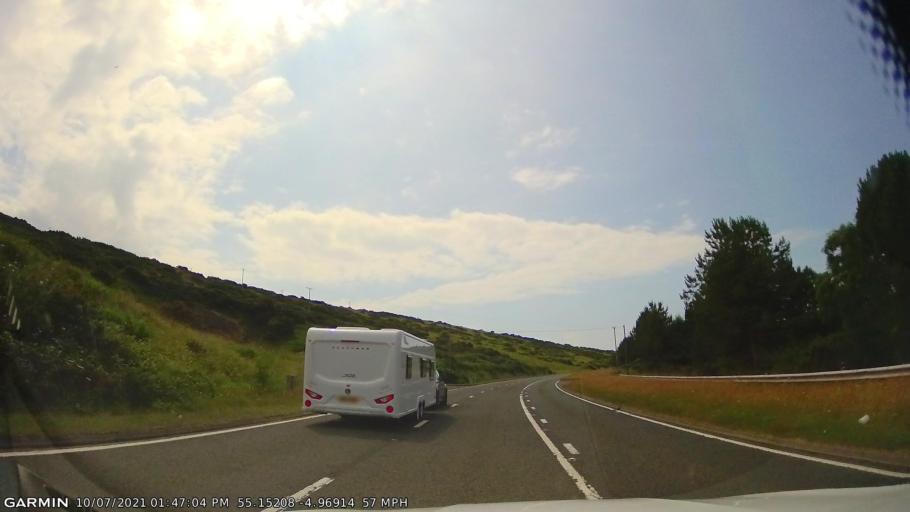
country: GB
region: Scotland
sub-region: South Ayrshire
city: Girvan
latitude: 55.1521
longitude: -4.9691
